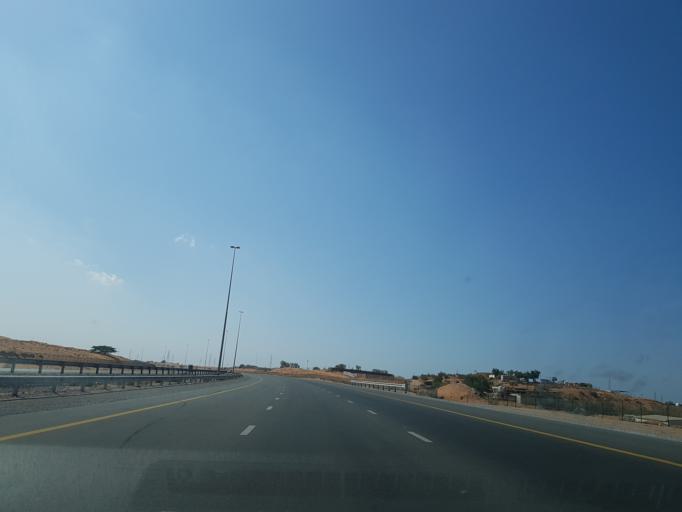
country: AE
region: Ra's al Khaymah
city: Ras al-Khaimah
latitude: 25.7057
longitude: 55.9469
